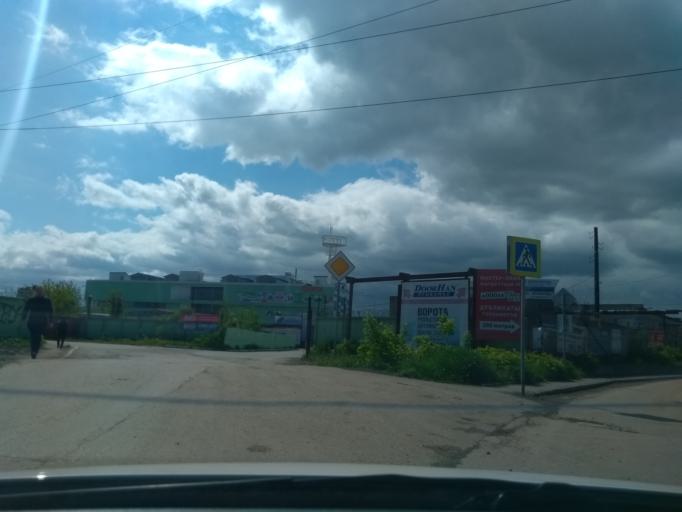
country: RU
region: Perm
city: Perm
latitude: 57.9815
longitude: 56.2436
